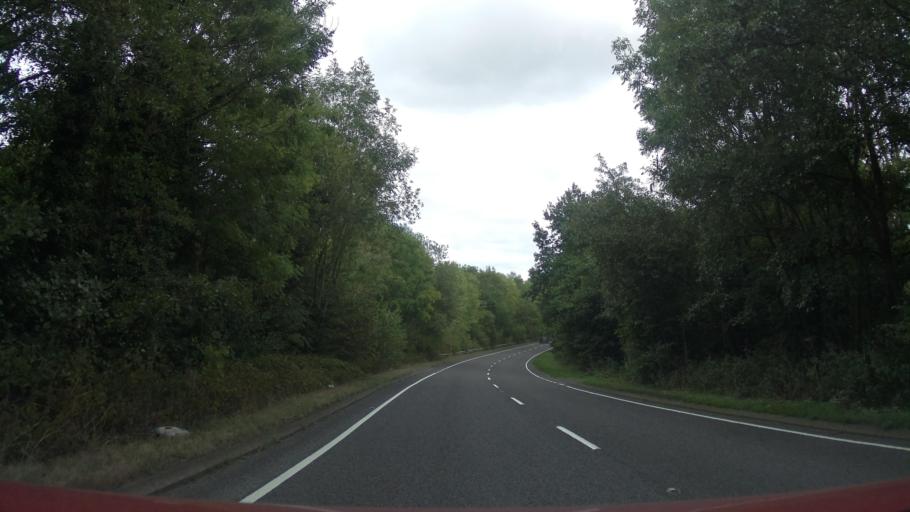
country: GB
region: England
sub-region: Leicestershire
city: Coalville
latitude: 52.7508
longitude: -1.4119
